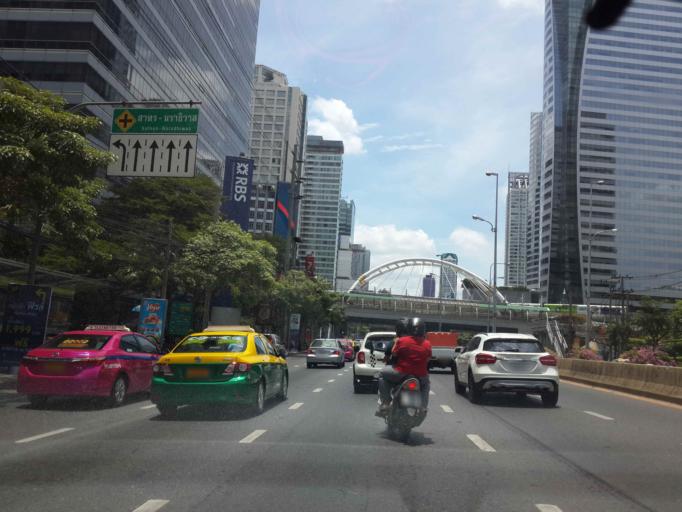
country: TH
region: Bangkok
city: Bang Rak
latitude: 13.7222
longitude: 100.5318
